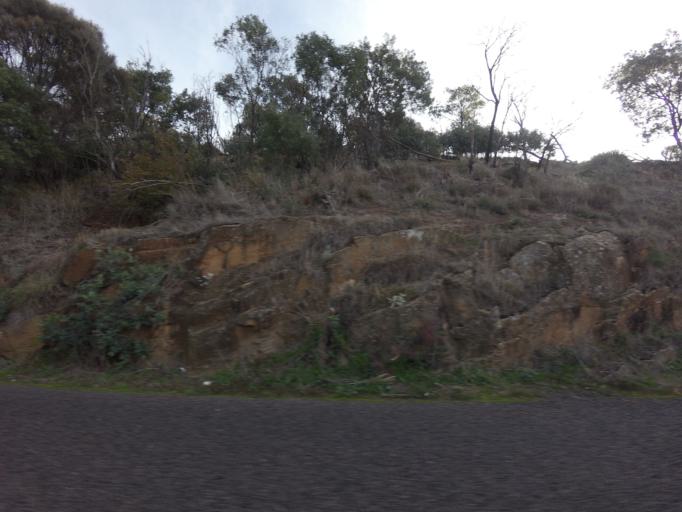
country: AU
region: Tasmania
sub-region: Brighton
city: Bridgewater
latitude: -42.4211
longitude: 147.1407
